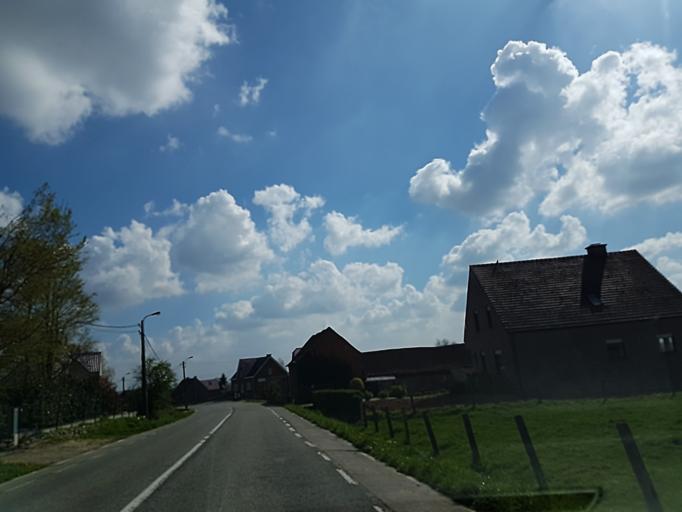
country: BE
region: Flanders
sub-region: Provincie Oost-Vlaanderen
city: Sint-Maria-Lierde
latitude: 50.8261
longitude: 3.8789
